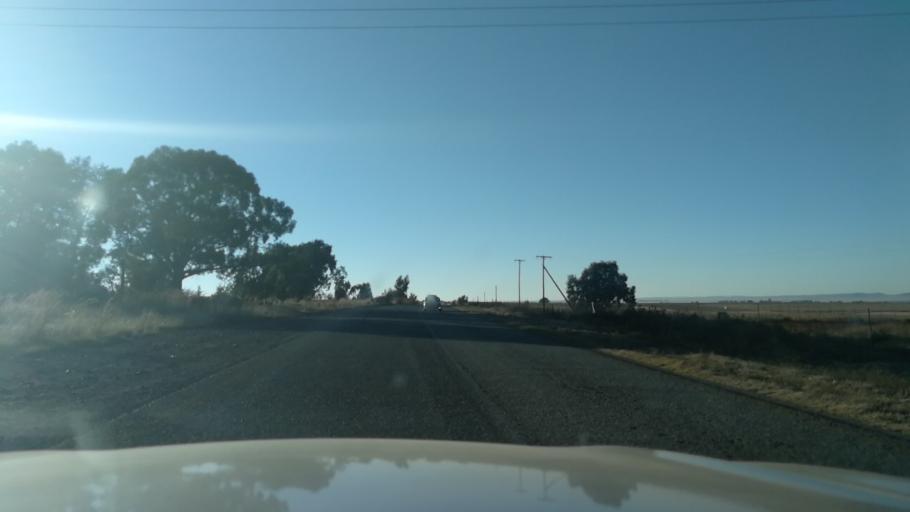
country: ZA
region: North-West
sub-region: Bojanala Platinum District Municipality
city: Koster
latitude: -25.9130
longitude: 27.0557
